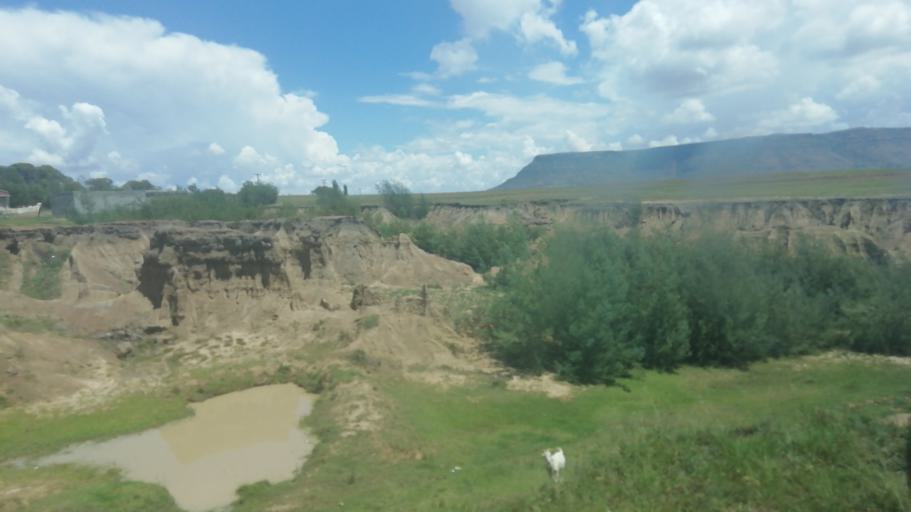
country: LS
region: Maseru
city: Nako
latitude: -29.6188
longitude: 27.5180
